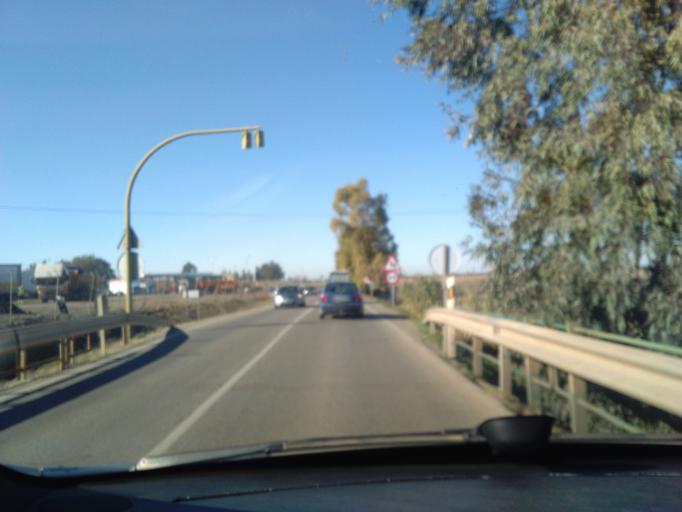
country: ES
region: Andalusia
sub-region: Provincia de Sevilla
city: Sevilla
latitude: 37.4299
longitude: -5.9320
